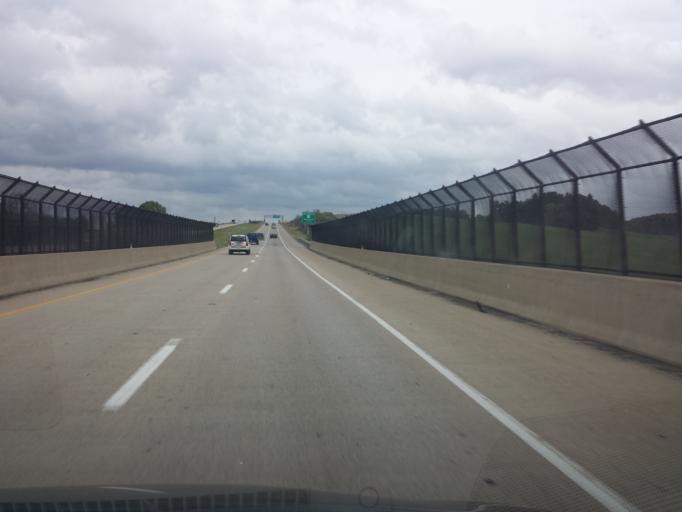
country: US
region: Pennsylvania
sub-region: Centre County
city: Pleasant Gap
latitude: 40.8619
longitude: -77.7891
